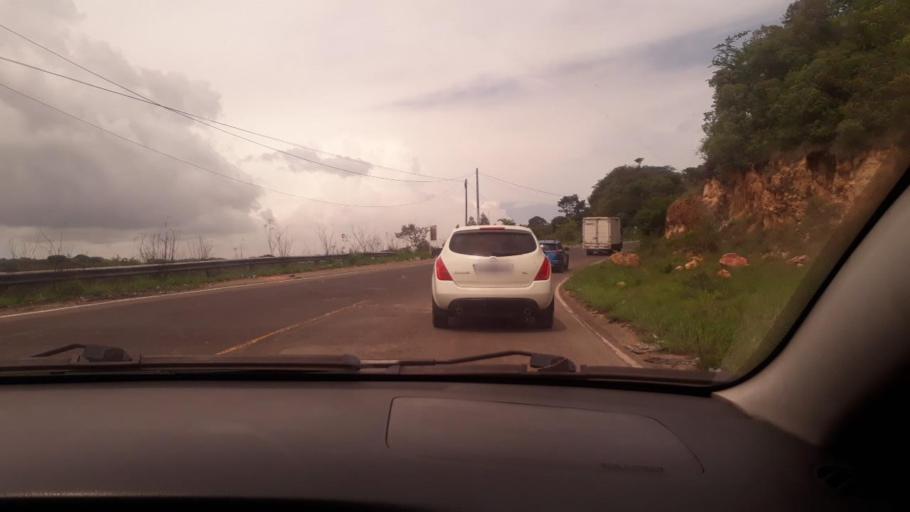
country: GT
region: Jutiapa
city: Quesada
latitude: 14.2779
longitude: -89.9899
